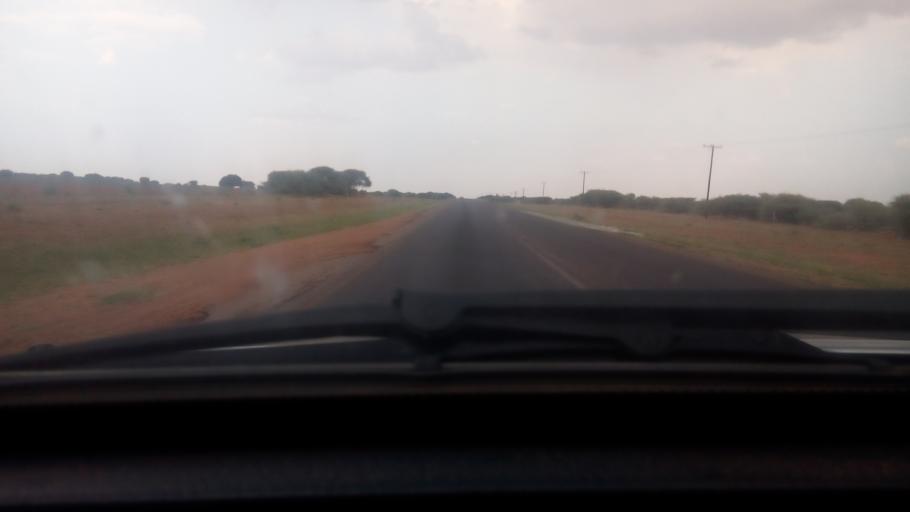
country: BW
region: Kweneng
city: Metsemotlhaba
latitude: -24.4694
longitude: 25.6860
